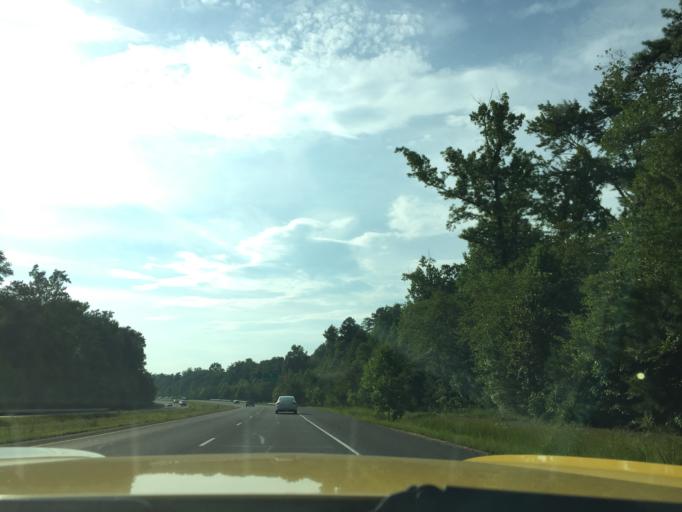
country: US
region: Virginia
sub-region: Fairfax County
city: Newington
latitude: 38.7202
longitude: -77.1708
